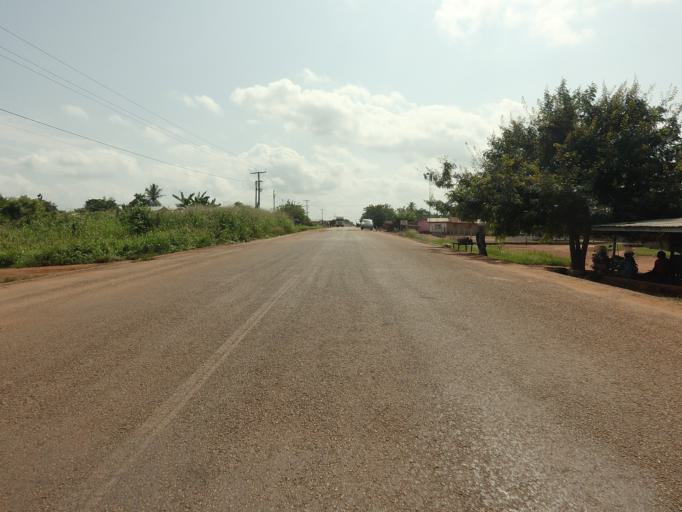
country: TG
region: Maritime
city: Tsevie
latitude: 6.3613
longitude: 0.8621
